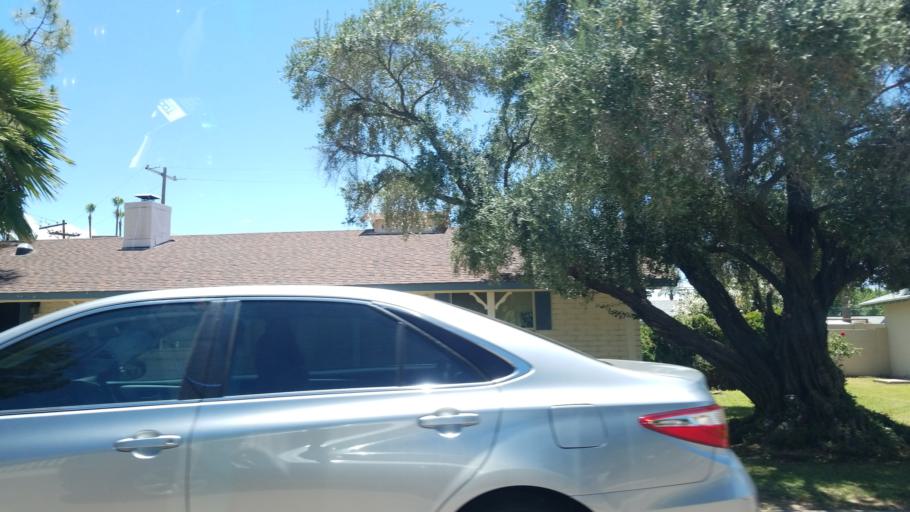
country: US
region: Arizona
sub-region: Maricopa County
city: Glendale
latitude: 33.5619
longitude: -112.0786
